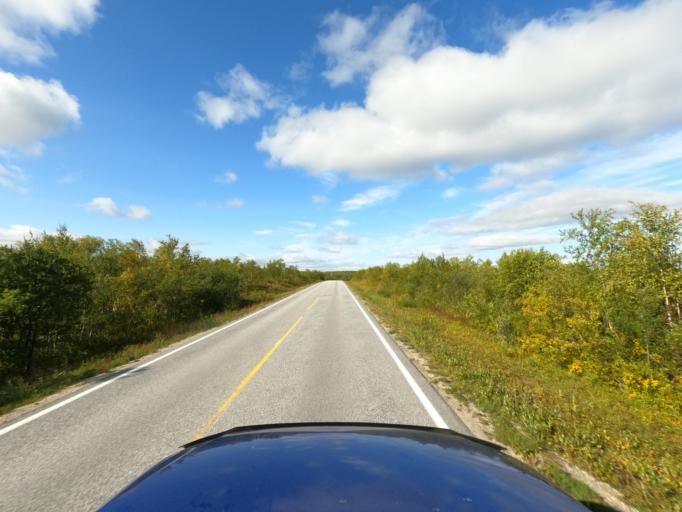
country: NO
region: Finnmark Fylke
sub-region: Karasjok
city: Karasjohka
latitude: 69.6093
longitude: 25.3150
